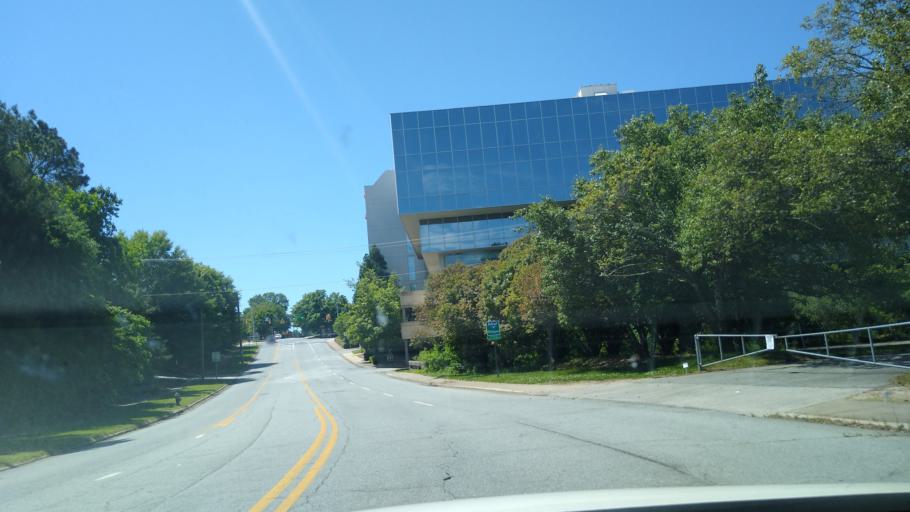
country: US
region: North Carolina
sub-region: Guilford County
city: Greensboro
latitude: 36.0894
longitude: -79.8331
